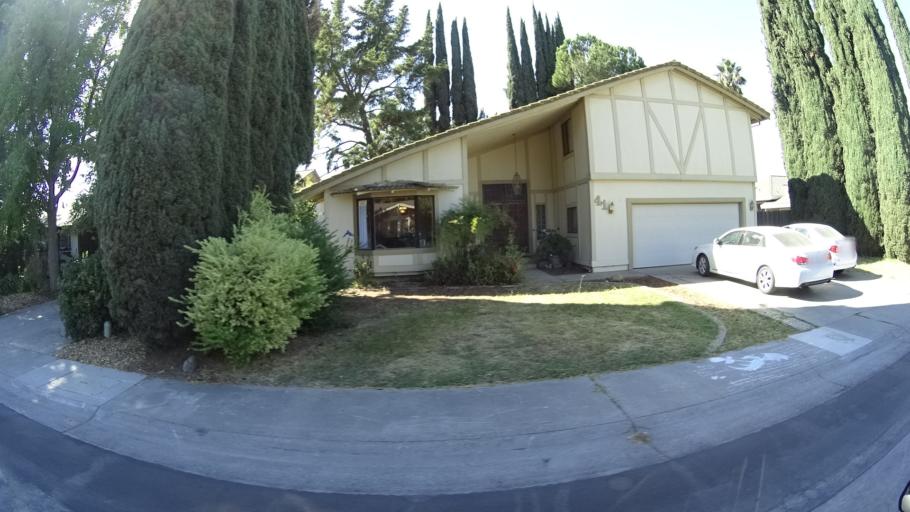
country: US
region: California
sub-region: Sacramento County
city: Parkway
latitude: 38.5029
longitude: -121.5316
